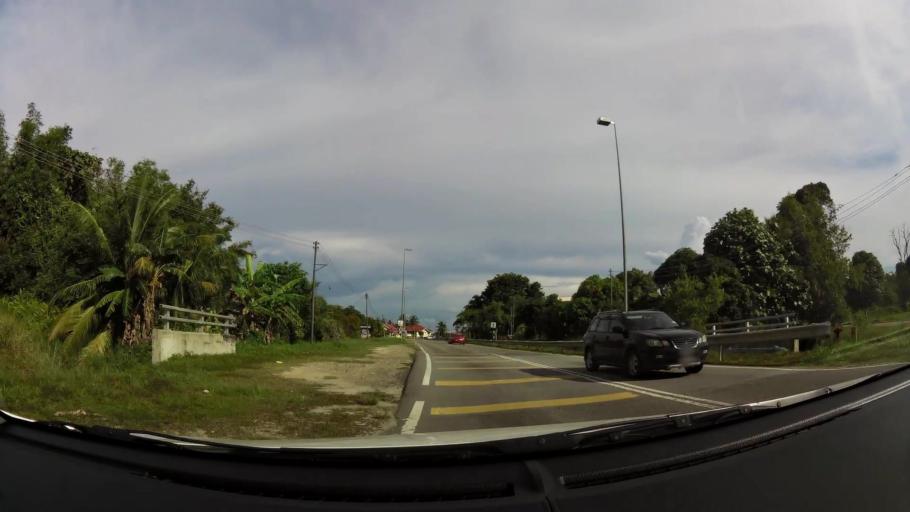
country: BN
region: Brunei and Muara
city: Bandar Seri Begawan
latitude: 4.9743
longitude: 115.0201
